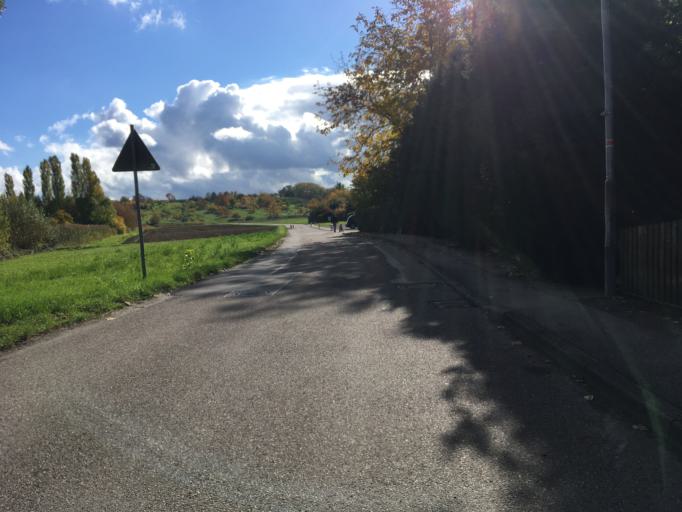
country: DE
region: Baden-Wuerttemberg
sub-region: Regierungsbezirk Stuttgart
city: Pfedelbach
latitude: 49.1778
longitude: 9.5092
